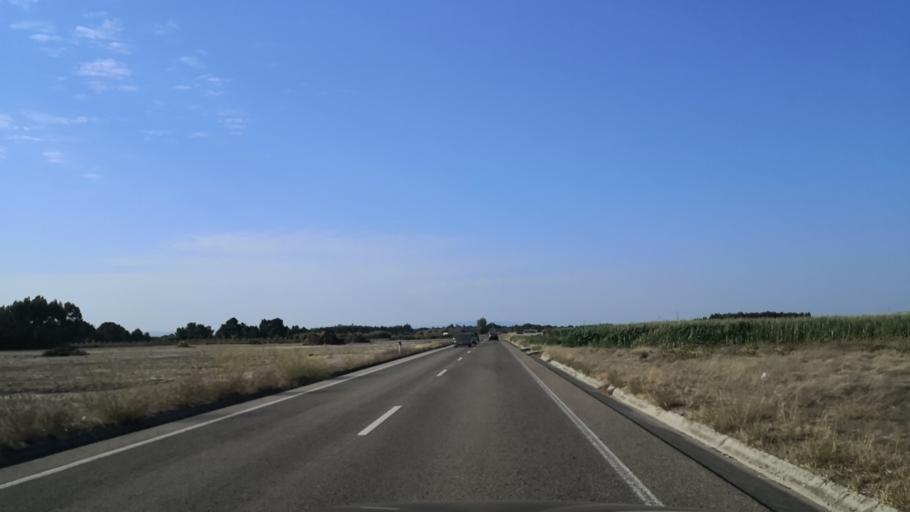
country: PT
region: Santarem
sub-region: Almeirim
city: Almeirim
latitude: 39.1631
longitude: -8.6204
